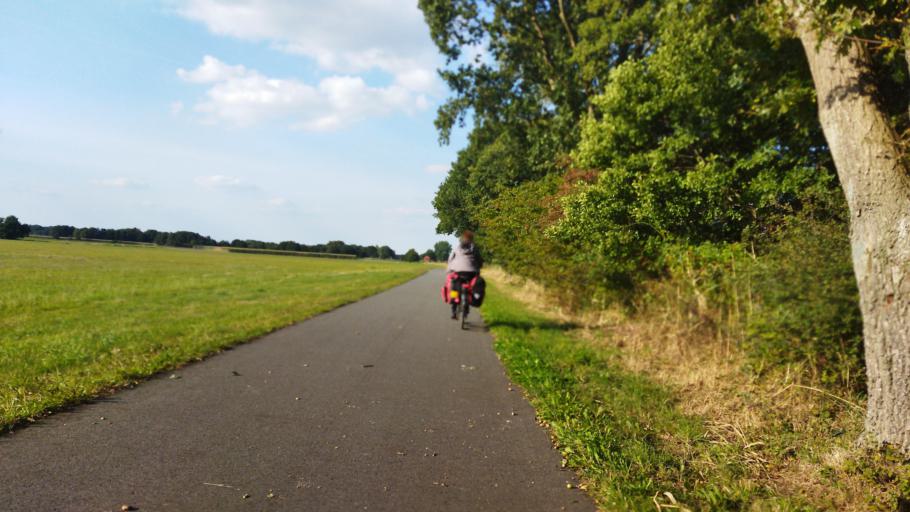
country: DE
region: Lower Saxony
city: Lehe
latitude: 53.0166
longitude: 7.3208
